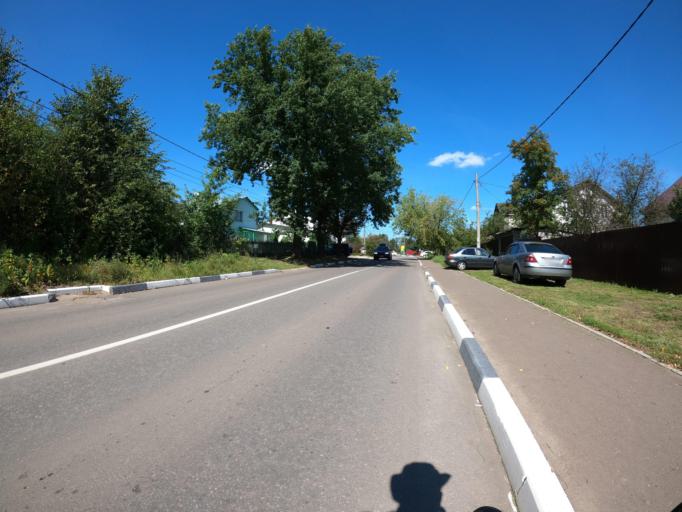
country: RU
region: Moskovskaya
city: Stupino
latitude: 54.8951
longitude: 38.0888
